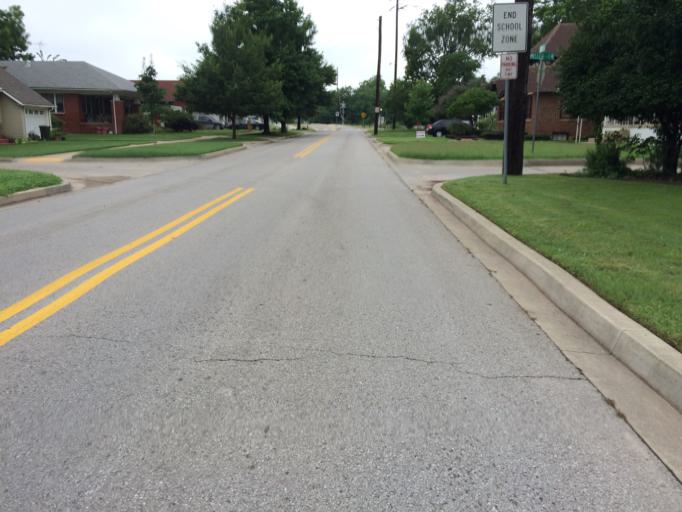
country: US
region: Oklahoma
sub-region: Cleveland County
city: Norman
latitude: 35.2153
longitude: -97.4384
